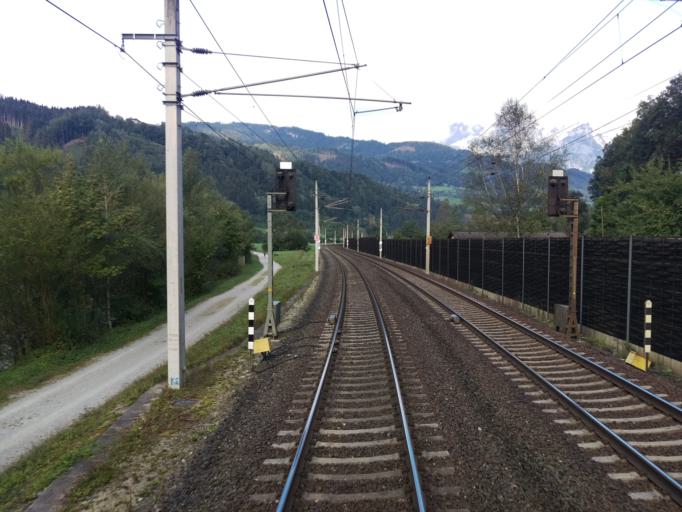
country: AT
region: Salzburg
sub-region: Politischer Bezirk Sankt Johann im Pongau
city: Pfarrwerfen
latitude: 47.4543
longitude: 13.2091
